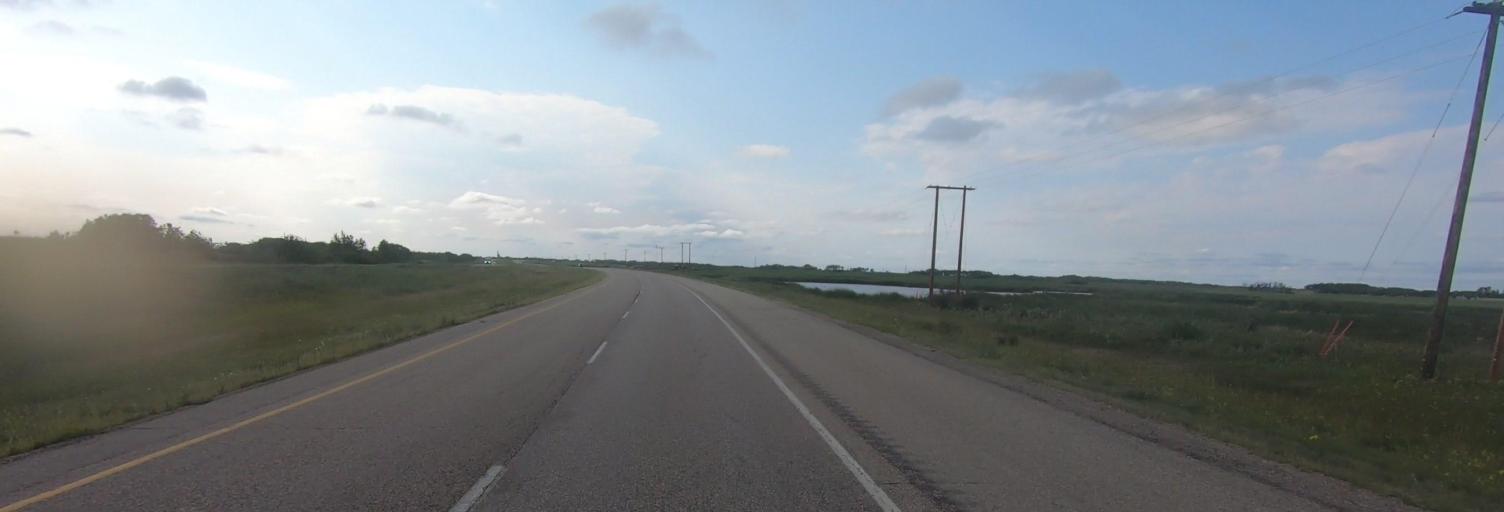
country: CA
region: Saskatchewan
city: Moosomin
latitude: 50.2524
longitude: -101.9208
